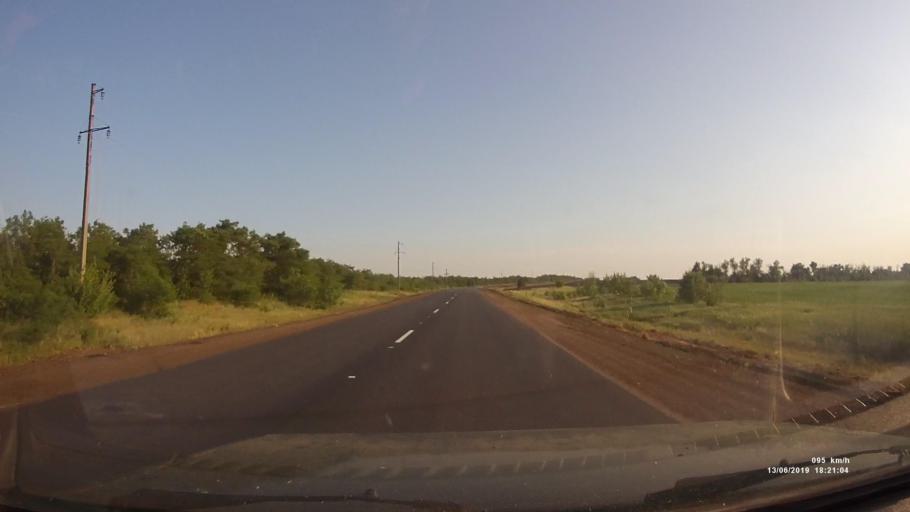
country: RU
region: Rostov
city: Kazanskaya
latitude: 49.8753
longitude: 41.2943
